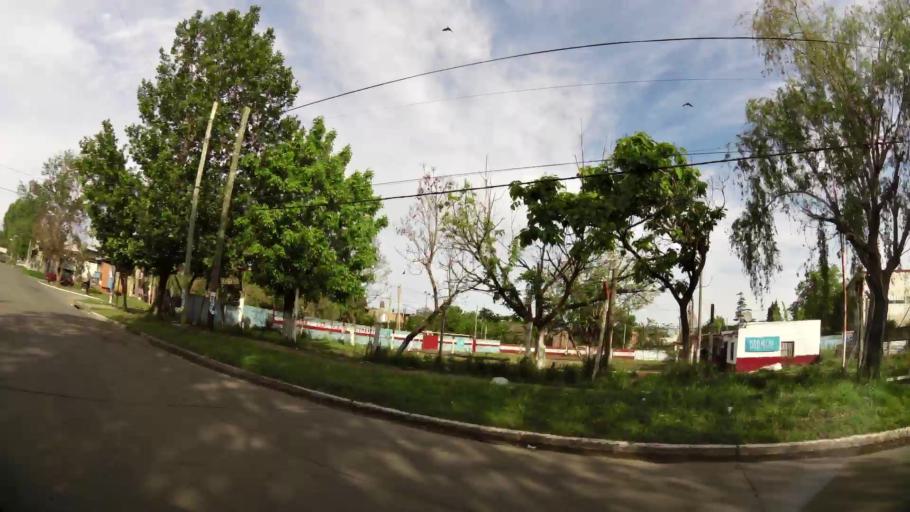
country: AR
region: Buenos Aires
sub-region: Partido de Quilmes
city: Quilmes
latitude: -34.7445
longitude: -58.2641
